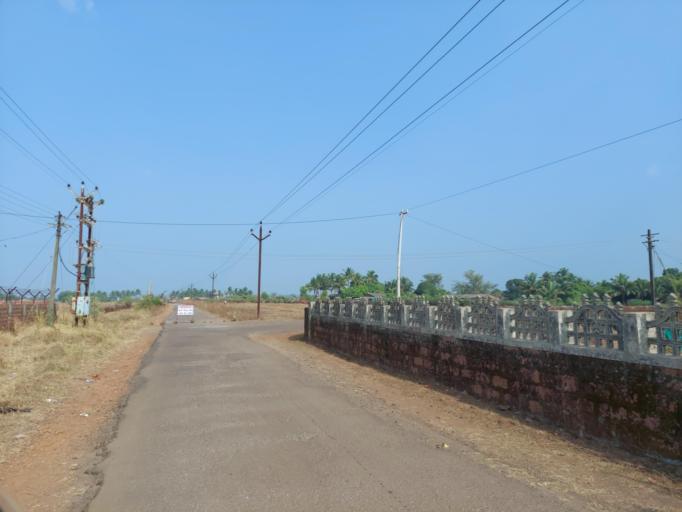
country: IN
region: Maharashtra
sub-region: Ratnagiri
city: Ratnagiri
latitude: 16.9241
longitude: 73.3166
